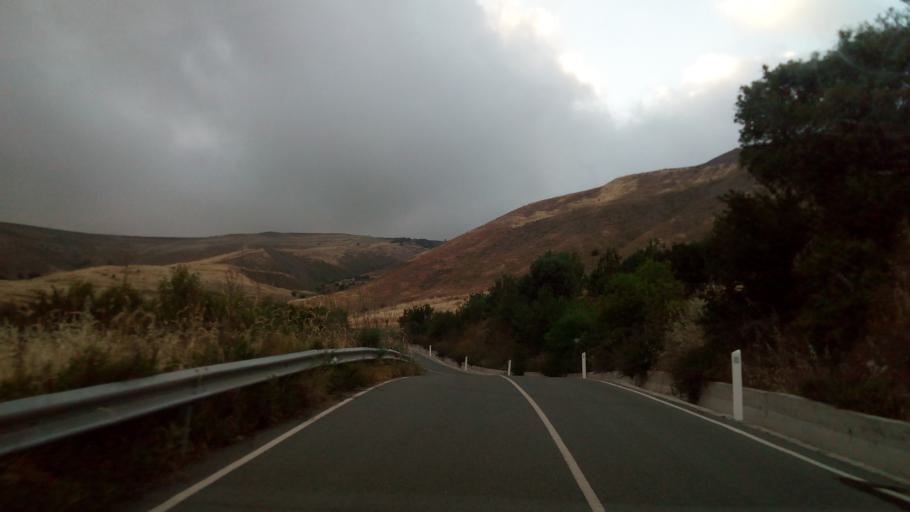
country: CY
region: Limassol
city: Pachna
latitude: 34.8690
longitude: 32.6331
